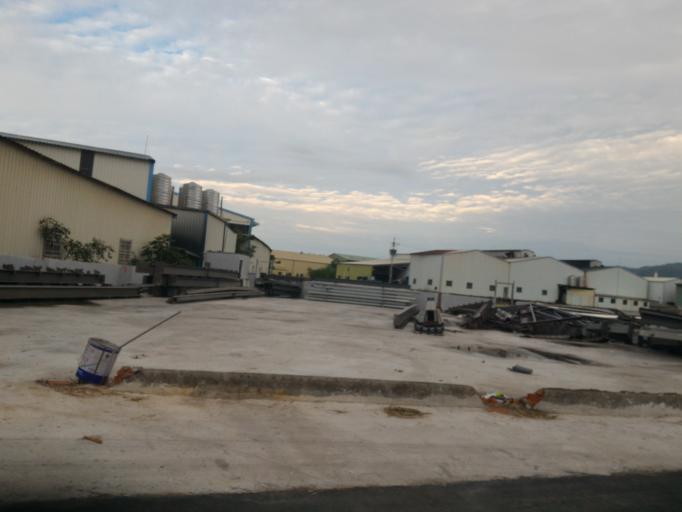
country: TW
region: Taipei
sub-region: Taipei
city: Banqiao
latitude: 24.9550
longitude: 121.4010
